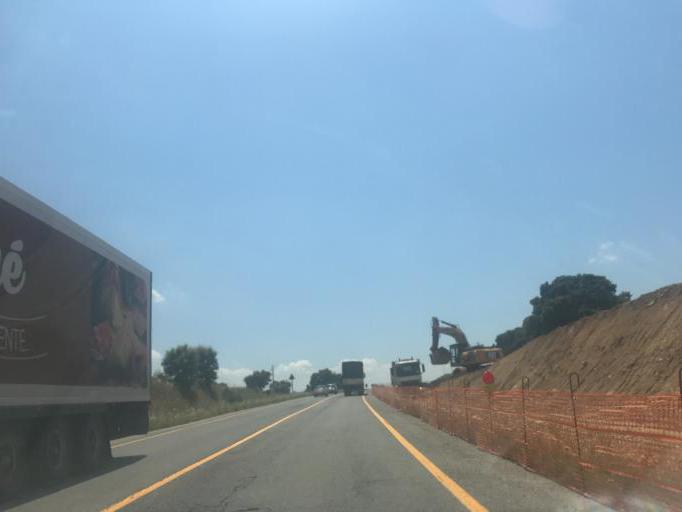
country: IT
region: Sardinia
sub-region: Provincia di Olbia-Tempio
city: Berchidda
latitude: 40.7817
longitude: 9.2470
